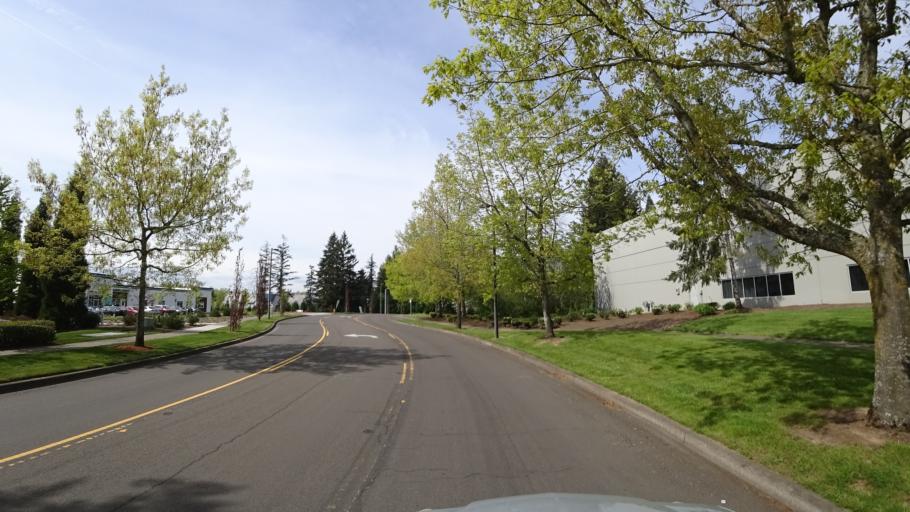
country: US
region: Oregon
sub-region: Washington County
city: Hillsboro
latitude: 45.5370
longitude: -122.9336
